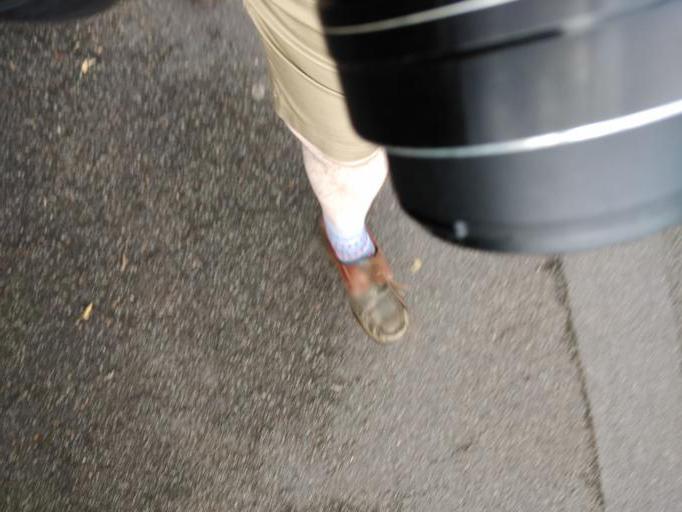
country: GB
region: England
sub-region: Nottingham
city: Nottingham
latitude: 52.9673
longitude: -1.2070
